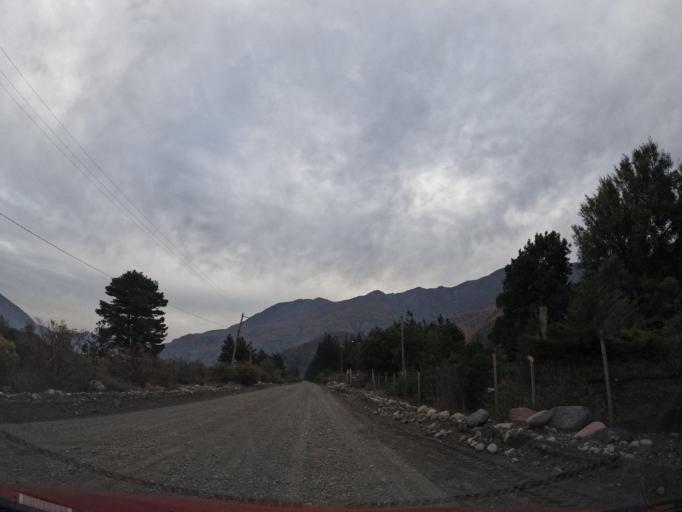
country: CL
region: Maule
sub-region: Provincia de Linares
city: Colbun
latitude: -35.7043
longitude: -71.0927
